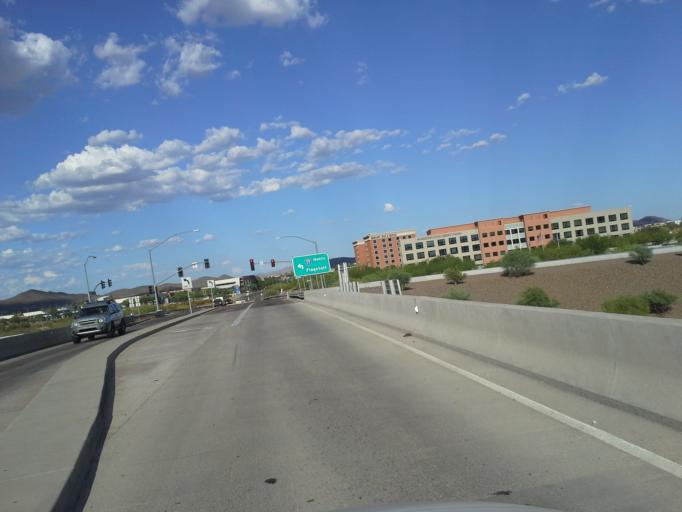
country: US
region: Arizona
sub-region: Maricopa County
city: Anthem
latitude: 33.6997
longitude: -112.1149
